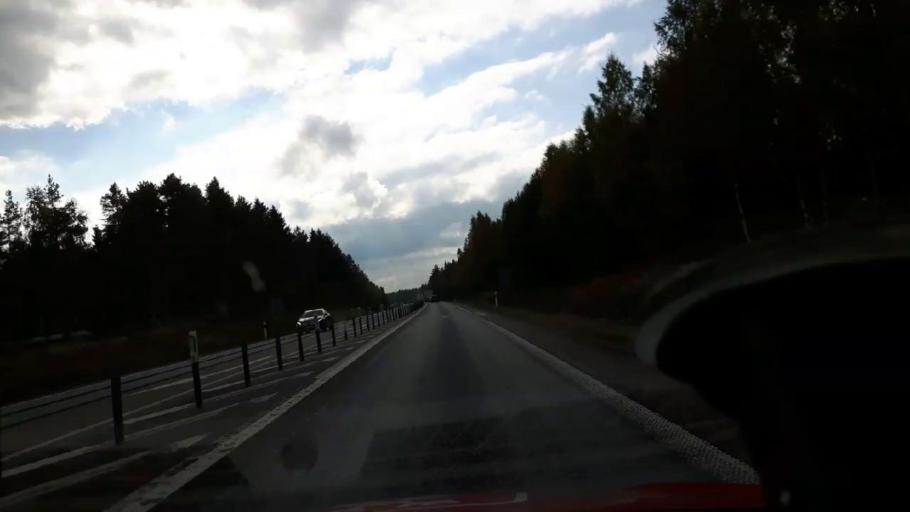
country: SE
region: Gaevleborg
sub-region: Gavle Kommun
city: Norrsundet
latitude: 60.9462
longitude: 17.0258
